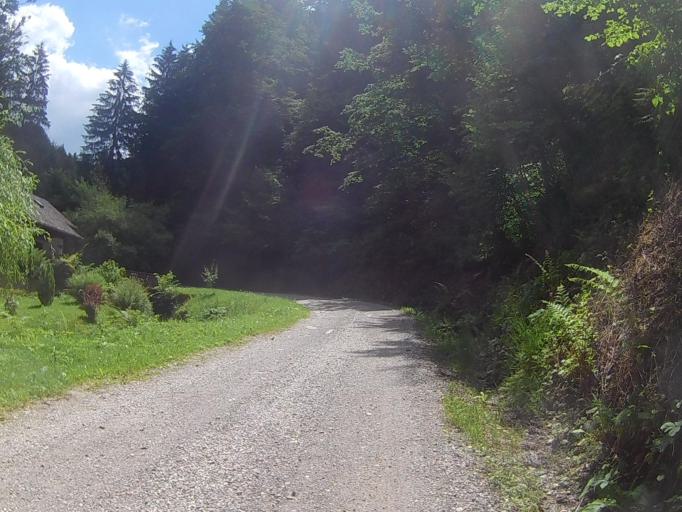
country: SI
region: Ruse
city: Ruse
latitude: 46.5290
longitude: 15.5003
